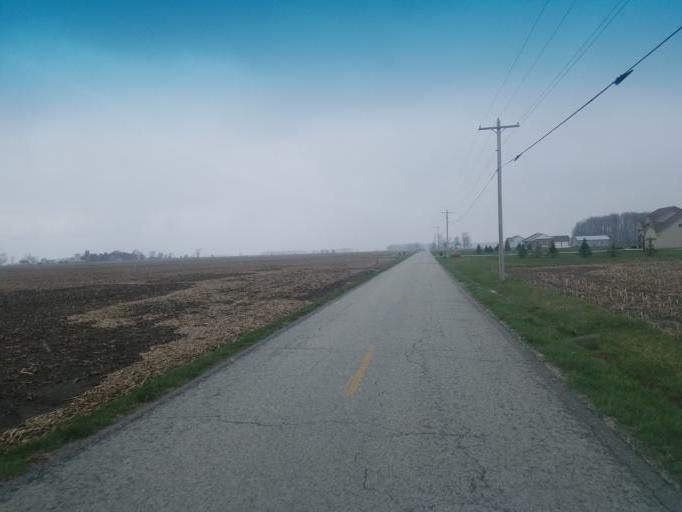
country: US
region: Ohio
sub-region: Marion County
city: Prospect
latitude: 40.3911
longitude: -83.1181
